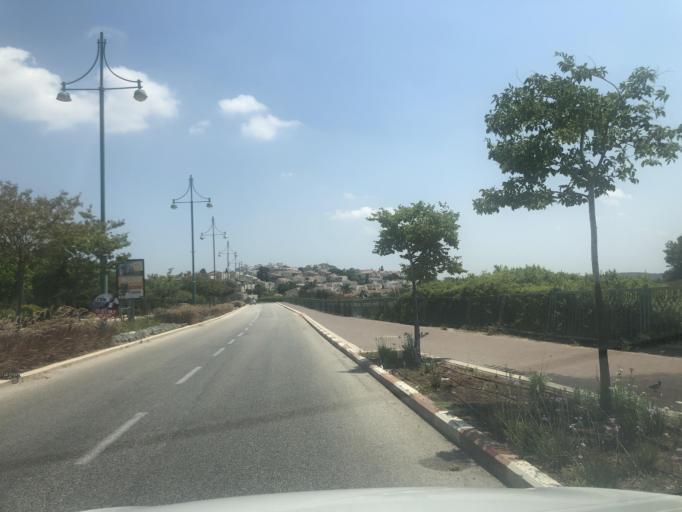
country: IL
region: Haifa
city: Daliyat el Karmil
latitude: 32.6358
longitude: 35.0816
